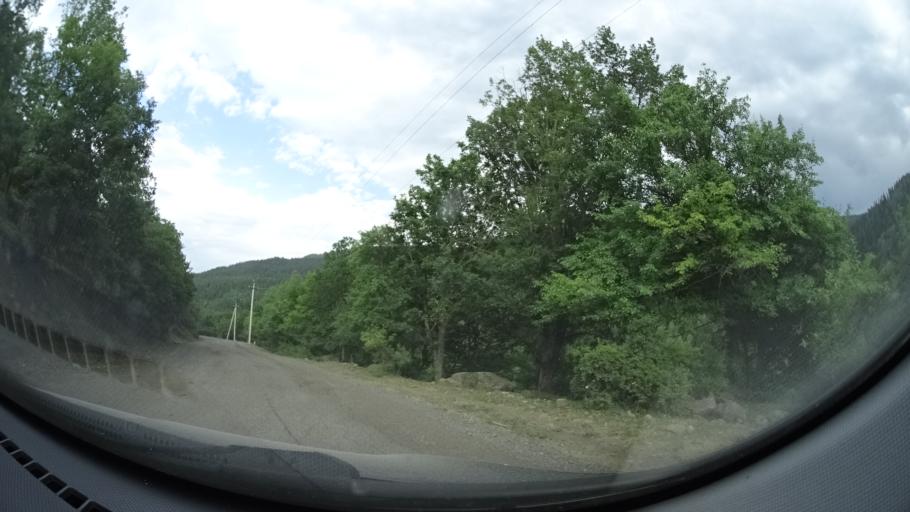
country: GE
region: Samtskhe-Javakheti
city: Adigeni
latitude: 41.6670
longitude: 42.6304
